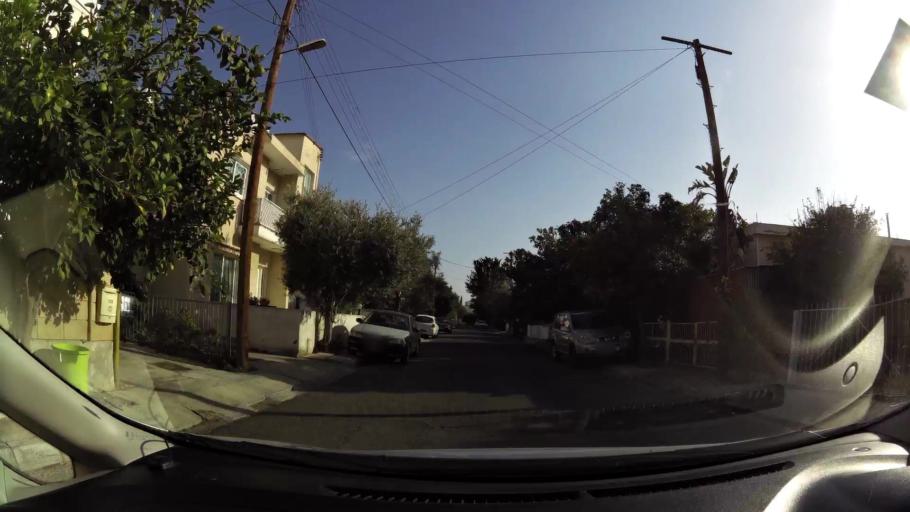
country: CY
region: Lefkosia
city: Nicosia
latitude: 35.1759
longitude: 33.3225
